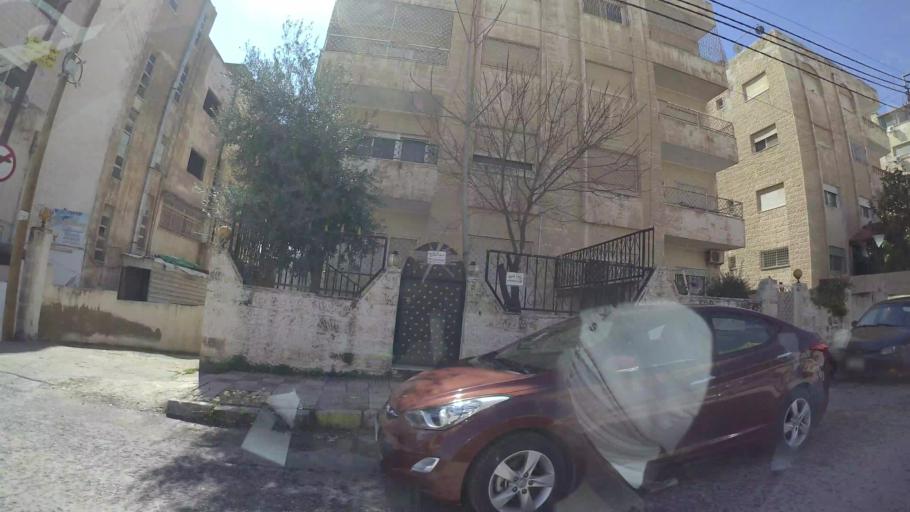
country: JO
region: Amman
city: Al Jubayhah
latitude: 31.9891
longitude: 35.9032
